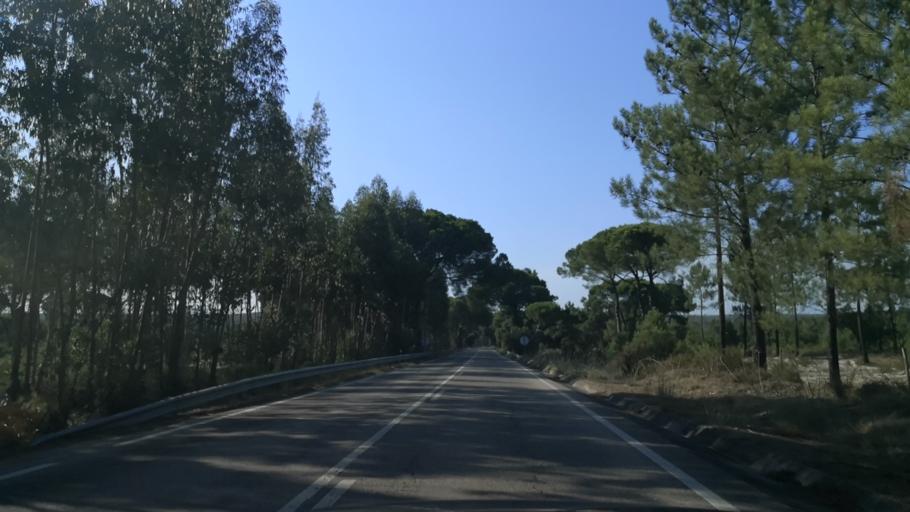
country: PT
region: Santarem
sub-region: Coruche
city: Coruche
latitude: 38.9842
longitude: -8.5485
